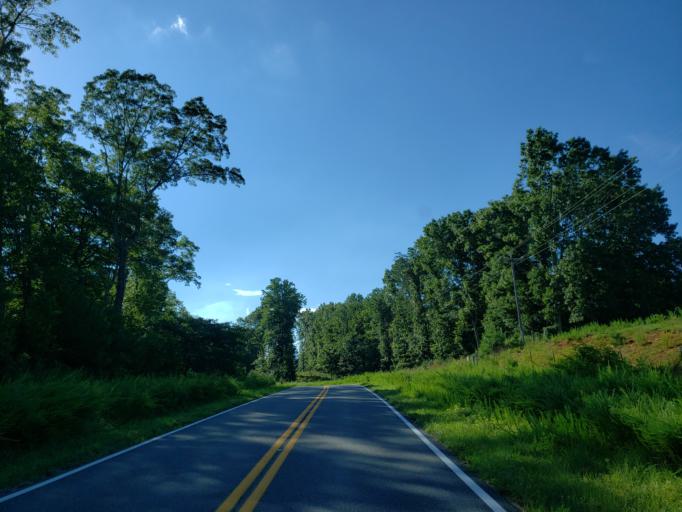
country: US
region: Georgia
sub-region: Bartow County
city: Rydal
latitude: 34.3523
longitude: -84.6002
